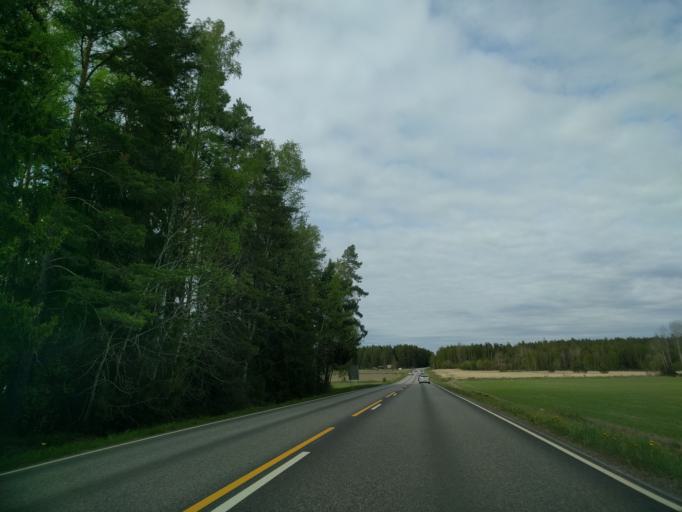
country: FI
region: Varsinais-Suomi
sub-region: Vakka-Suomi
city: Taivassalo
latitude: 60.5788
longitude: 21.6390
